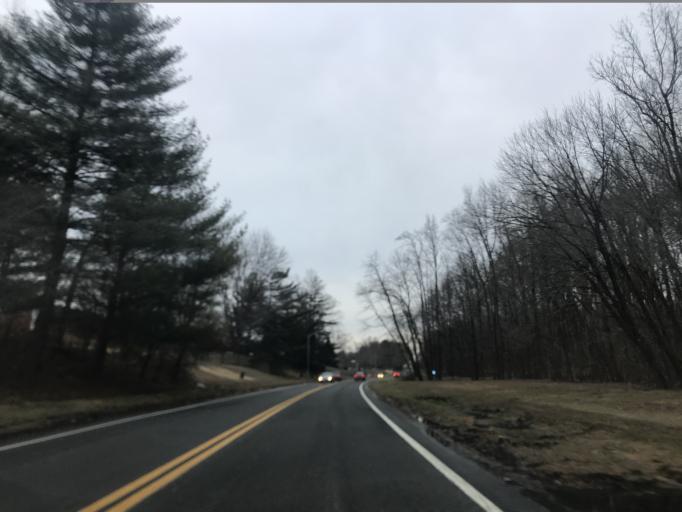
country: US
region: Maryland
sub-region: Prince George's County
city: Kettering
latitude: 38.8926
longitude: -76.7855
